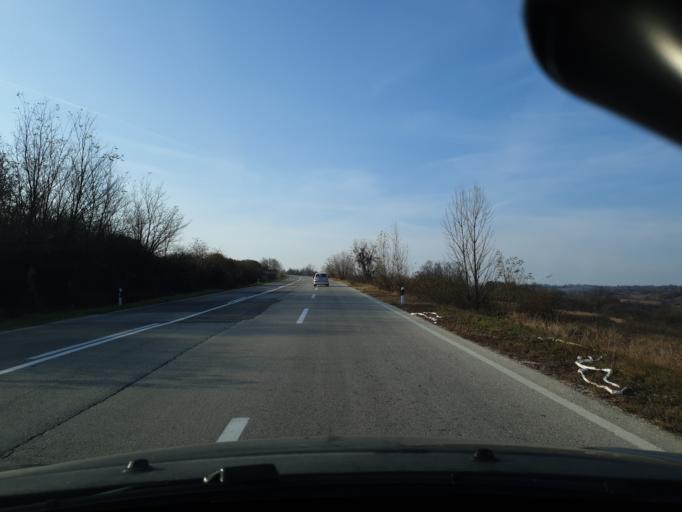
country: RS
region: Central Serbia
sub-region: Zajecarski Okrug
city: Zajecar
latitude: 43.9578
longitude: 22.2720
